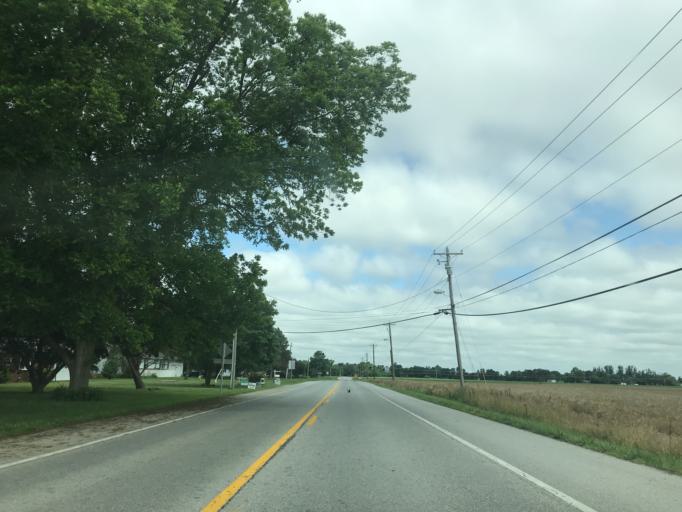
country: US
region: Maryland
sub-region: Caroline County
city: Ridgely
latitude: 38.9547
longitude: -75.8868
